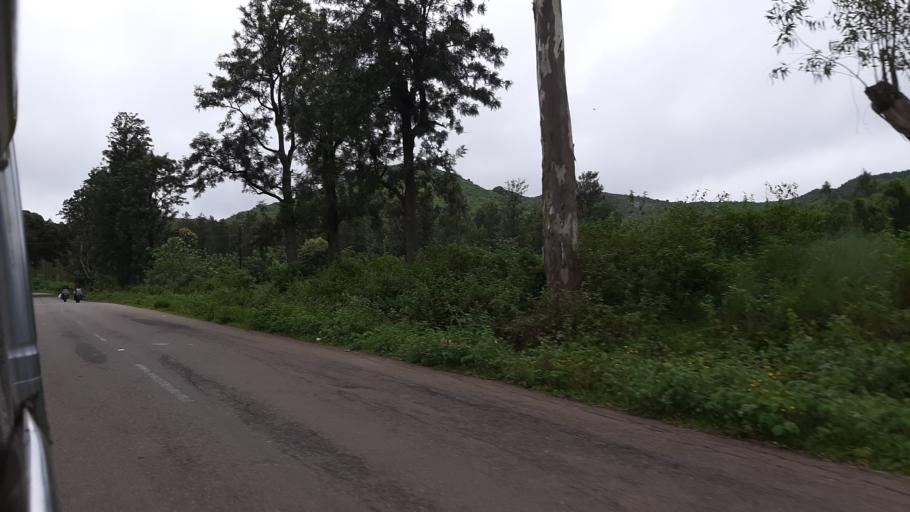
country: IN
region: Andhra Pradesh
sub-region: Vizianagaram District
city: Salur
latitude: 18.2874
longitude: 82.9330
